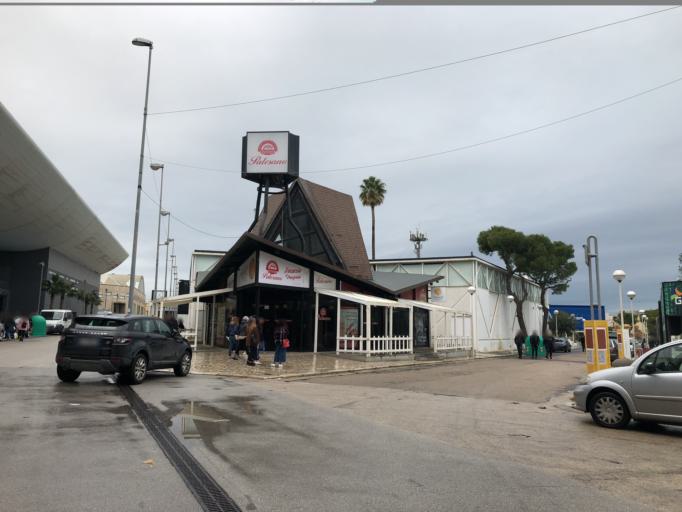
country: IT
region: Apulia
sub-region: Provincia di Bari
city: Bari
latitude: 41.1356
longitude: 16.8394
